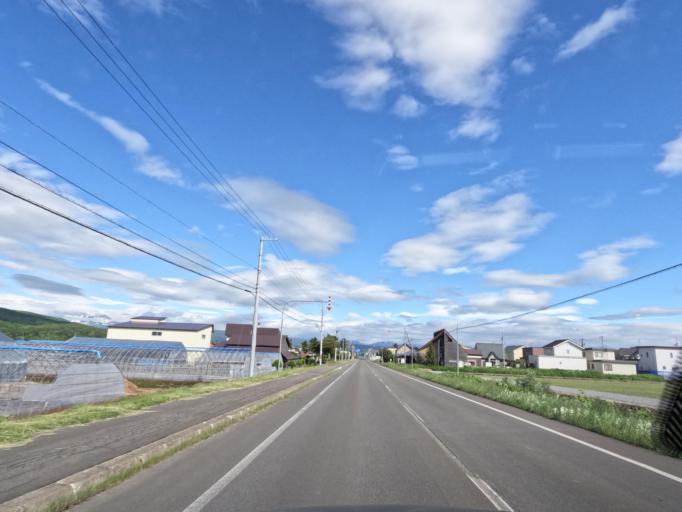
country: JP
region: Hokkaido
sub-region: Asahikawa-shi
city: Asahikawa
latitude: 43.7196
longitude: 142.5248
